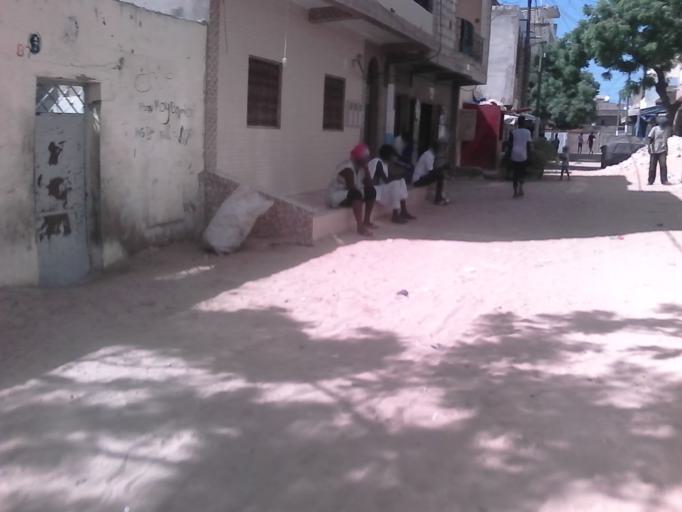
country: SN
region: Dakar
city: Grand Dakar
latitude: 14.7086
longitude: -17.4542
